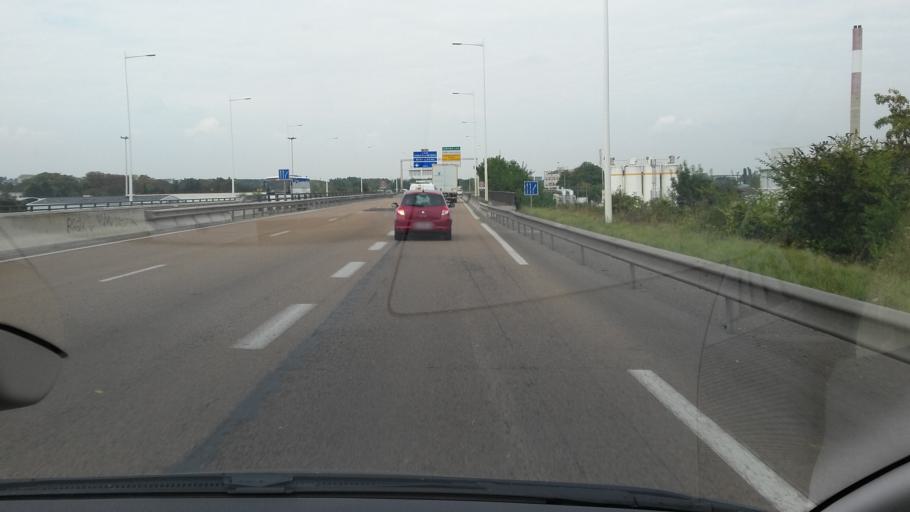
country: FR
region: Champagne-Ardenne
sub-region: Departement de la Marne
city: Cormontreuil
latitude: 49.2274
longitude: 4.0671
